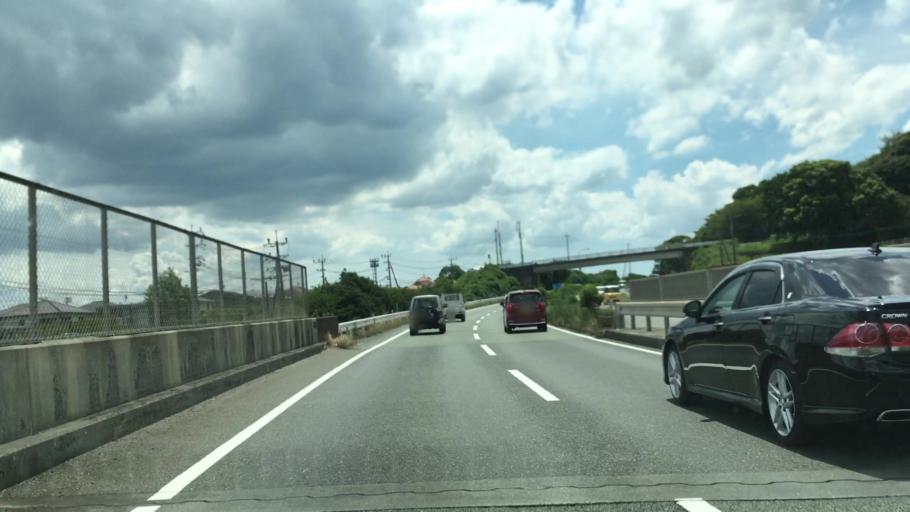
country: JP
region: Saga Prefecture
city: Tosu
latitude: 33.4033
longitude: 130.5134
